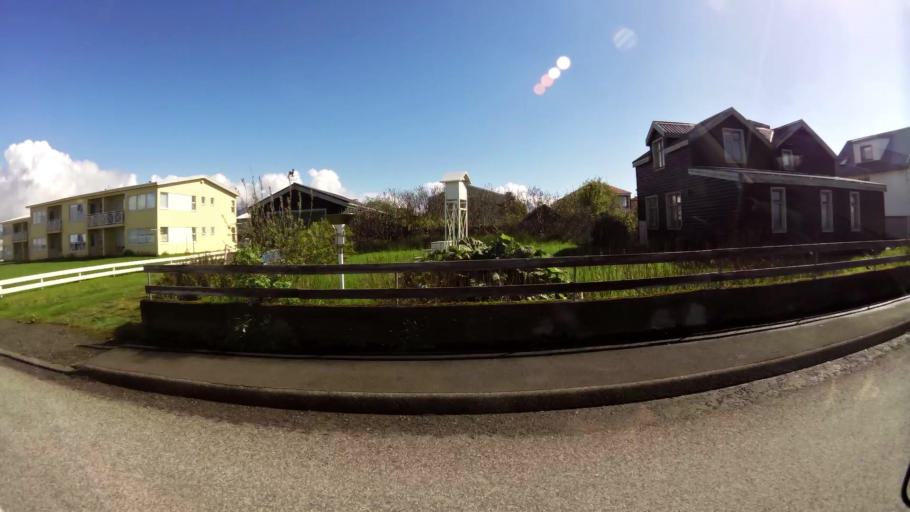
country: IS
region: East
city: Hoefn
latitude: 64.2509
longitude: -15.2136
